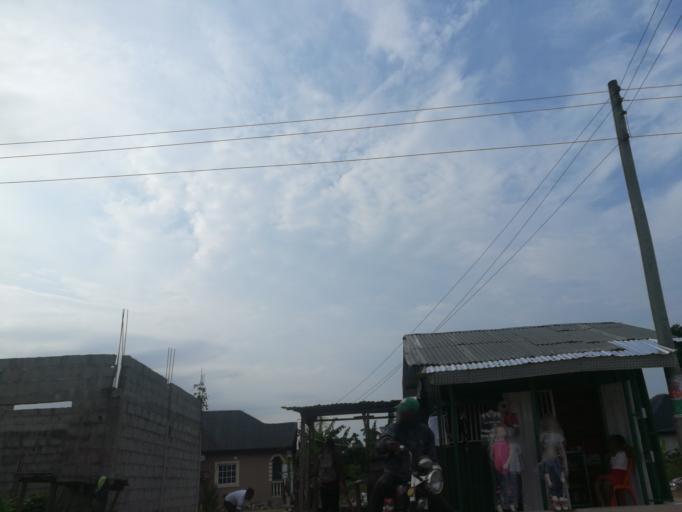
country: NG
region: Rivers
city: Okrika
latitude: 4.7610
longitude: 7.0907
